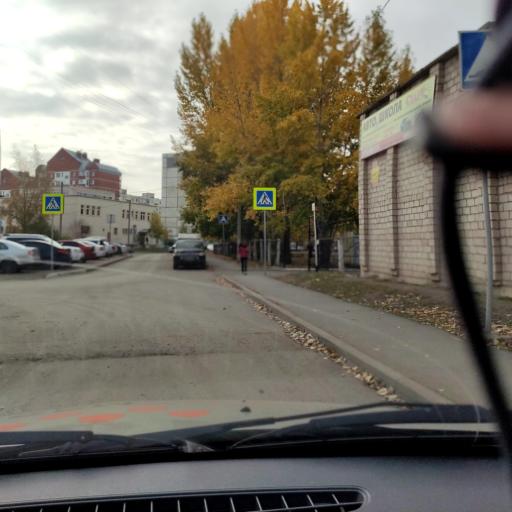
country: RU
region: Bashkortostan
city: Ufa
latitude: 54.7700
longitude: 56.0812
